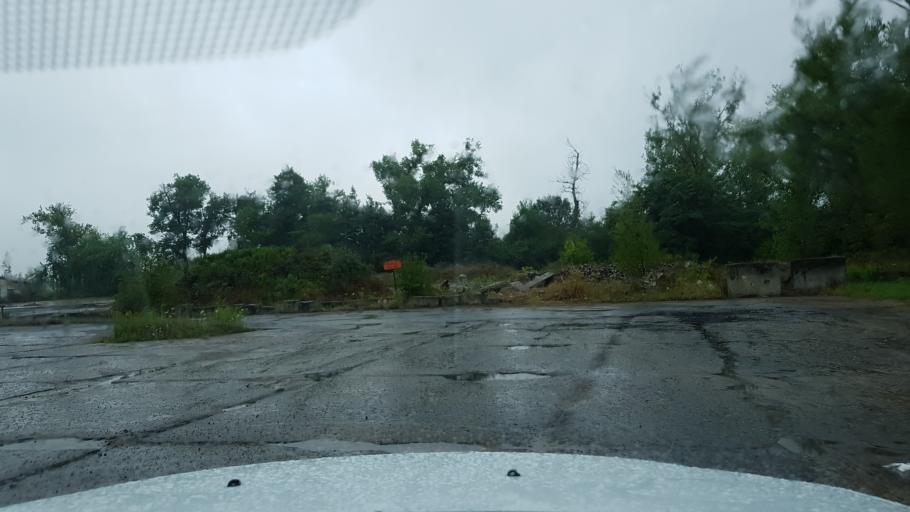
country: PL
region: West Pomeranian Voivodeship
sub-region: Powiat gryfinski
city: Chojna
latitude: 52.9462
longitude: 14.4212
